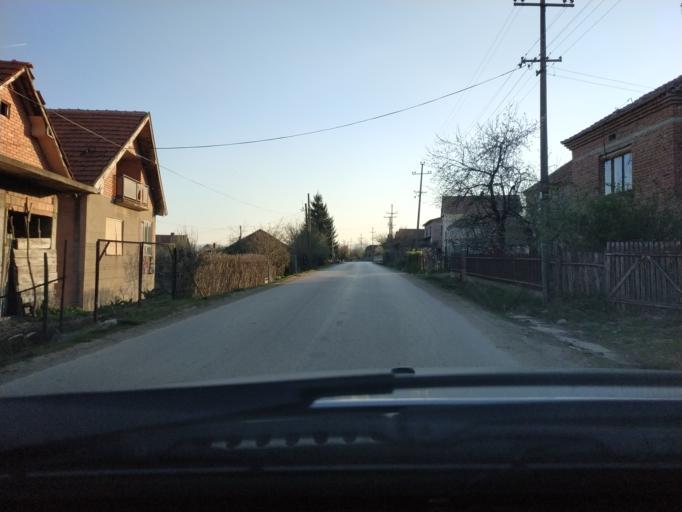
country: RS
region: Central Serbia
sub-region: Nisavski Okrug
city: Aleksinac
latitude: 43.5055
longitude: 21.7955
